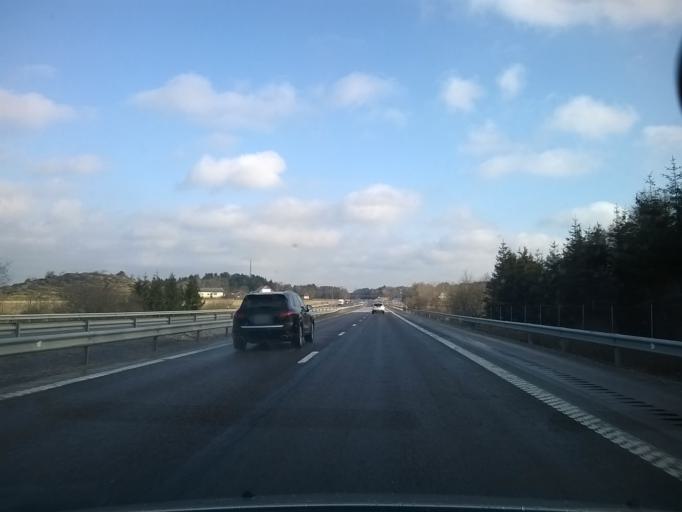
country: SE
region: Vaestra Goetaland
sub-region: Stenungsunds Kommun
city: Stora Hoga
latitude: 57.9769
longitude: 11.8404
